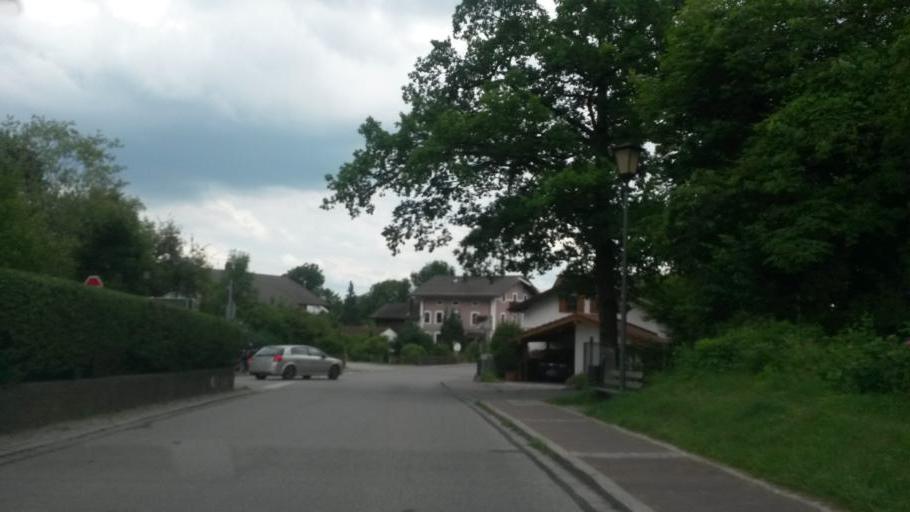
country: DE
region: Bavaria
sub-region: Upper Bavaria
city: Eggstatt
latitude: 47.9262
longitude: 12.3800
